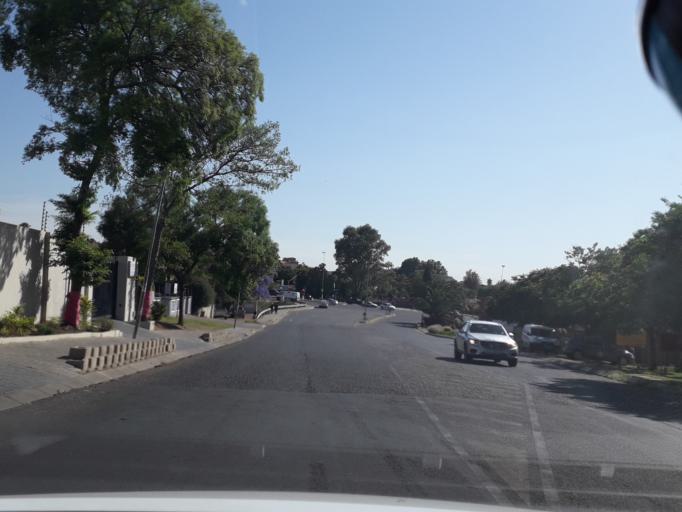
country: ZA
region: Gauteng
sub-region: City of Johannesburg Metropolitan Municipality
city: Roodepoort
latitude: -26.0875
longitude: 27.9338
